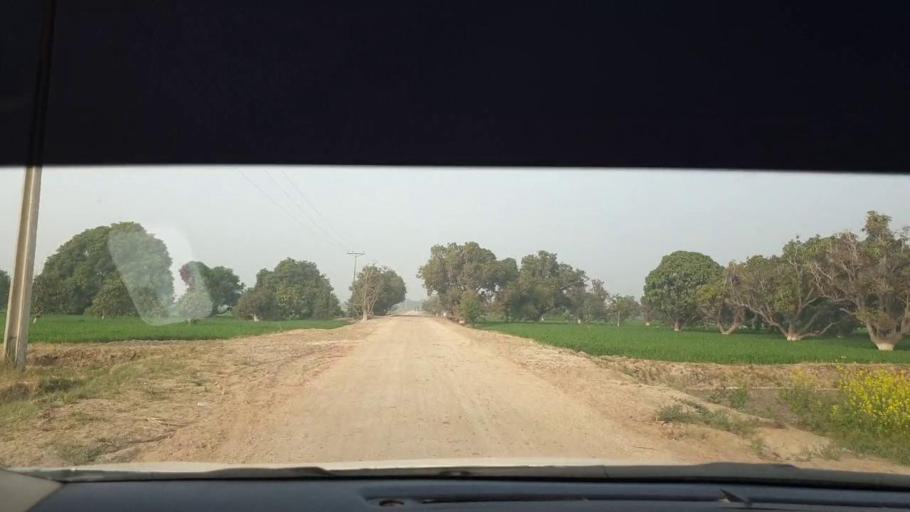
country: PK
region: Sindh
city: Berani
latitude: 25.7962
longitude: 68.8520
